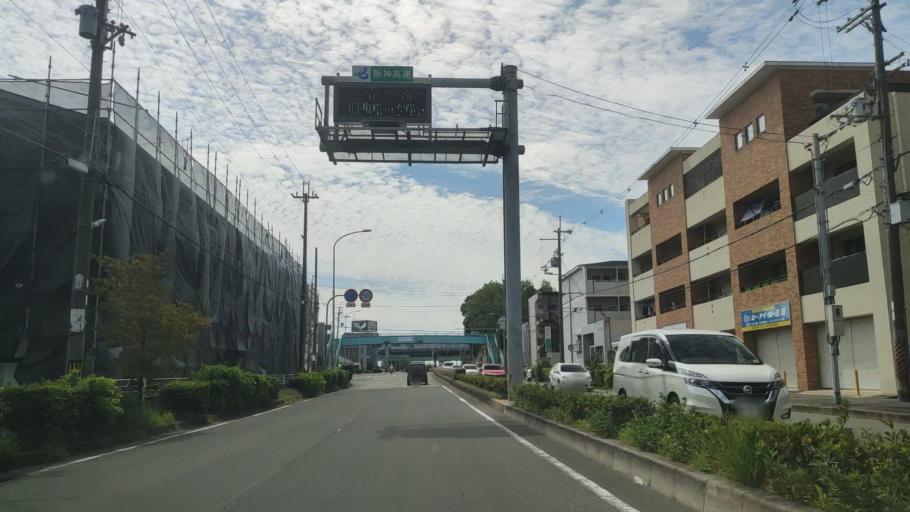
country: JP
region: Osaka
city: Ikeda
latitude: 34.8033
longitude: 135.4406
